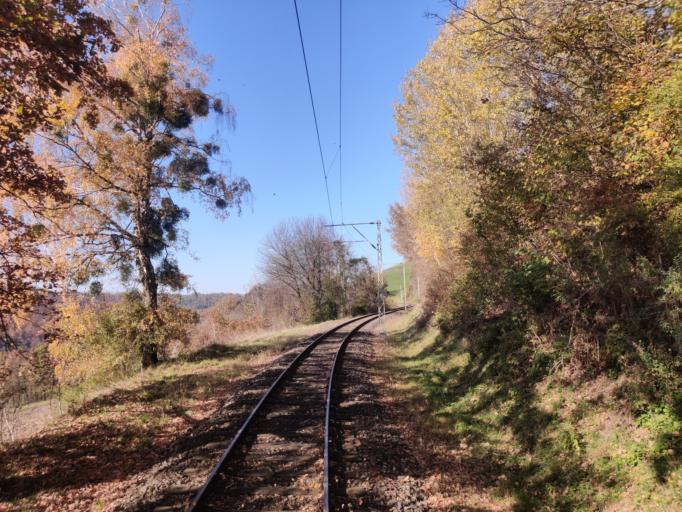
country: AT
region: Styria
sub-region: Politischer Bezirk Suedoststeiermark
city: Trautmannsdorf in Oststeiermark
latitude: 46.8863
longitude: 15.8799
